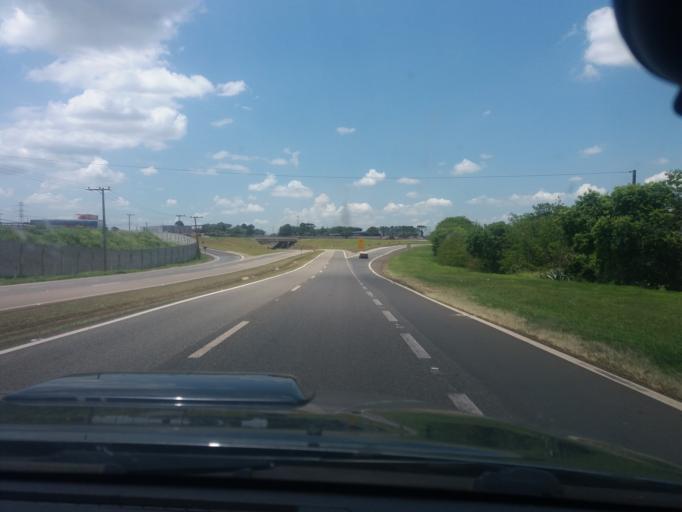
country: BR
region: Sao Paulo
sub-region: Itapetininga
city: Itapetininga
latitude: -23.5890
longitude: -47.9854
